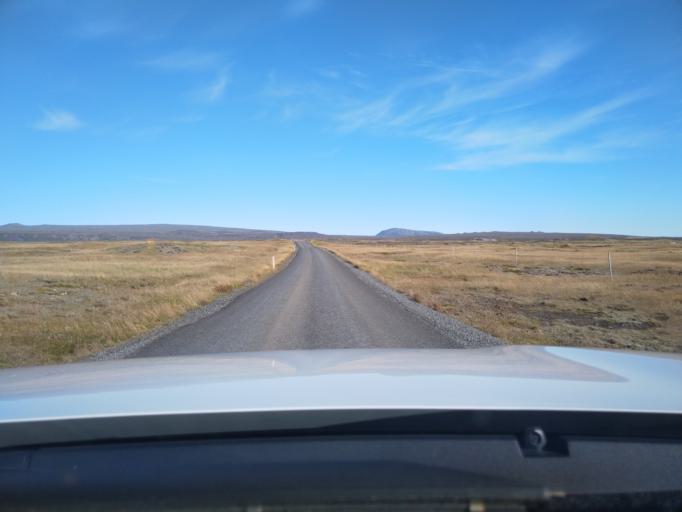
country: IS
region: South
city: THorlakshoefn
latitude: 63.8311
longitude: -21.6754
